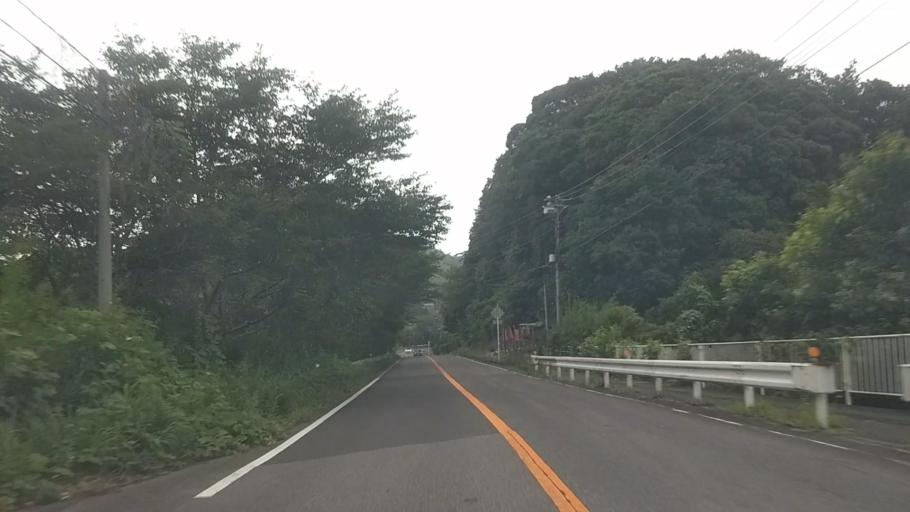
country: JP
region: Chiba
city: Katsuura
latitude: 35.2486
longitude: 140.1951
